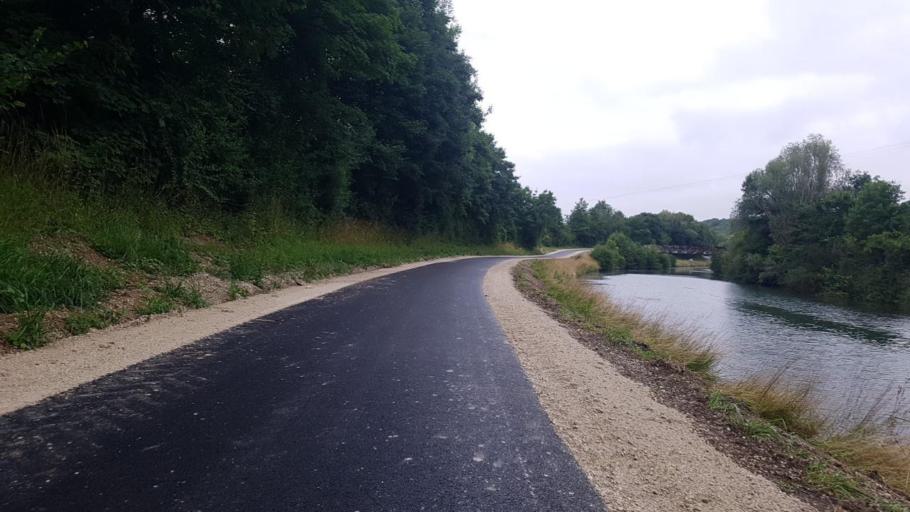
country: FR
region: Champagne-Ardenne
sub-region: Departement de la Marne
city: Vitry-le-Francois
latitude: 48.7618
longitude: 4.5629
